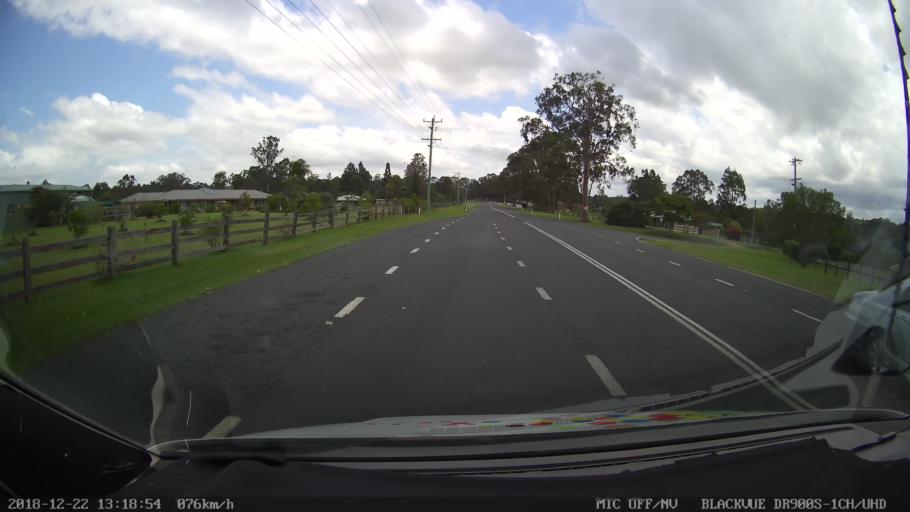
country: AU
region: New South Wales
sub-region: Clarence Valley
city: South Grafton
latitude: -29.7514
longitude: 152.9317
